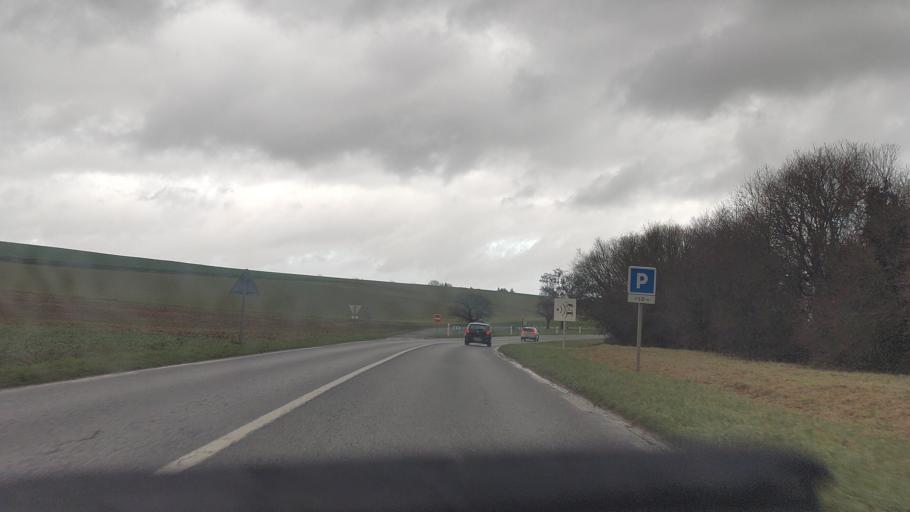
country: FR
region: Picardie
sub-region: Departement de l'Oise
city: Saint-Omer-en-Chaussee
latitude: 49.5847
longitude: 1.9534
